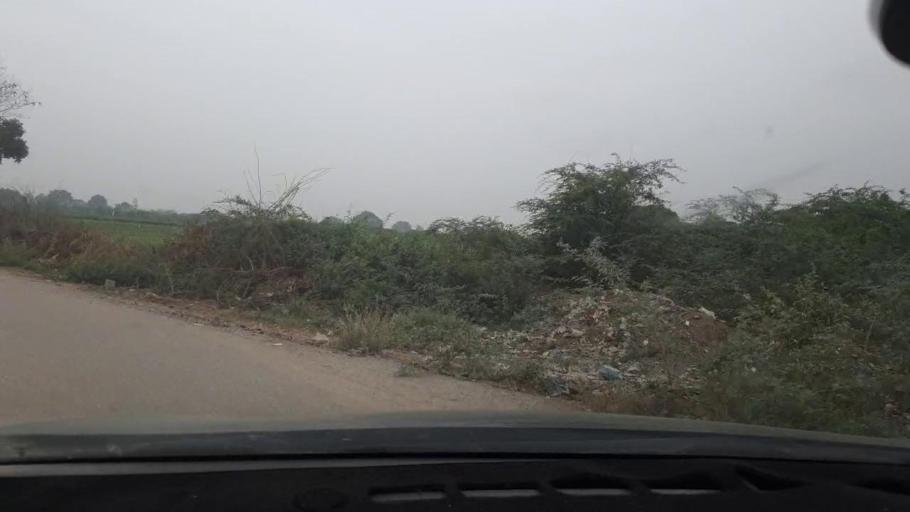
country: PK
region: Sindh
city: Malir Cantonment
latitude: 24.9258
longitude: 67.3214
